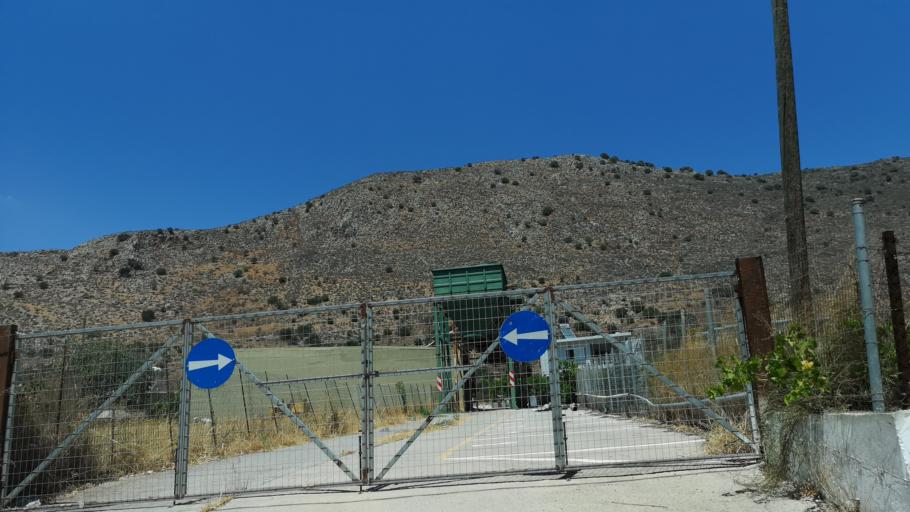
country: GR
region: Crete
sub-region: Nomos Lasithiou
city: Neapoli
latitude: 35.2459
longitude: 25.6391
